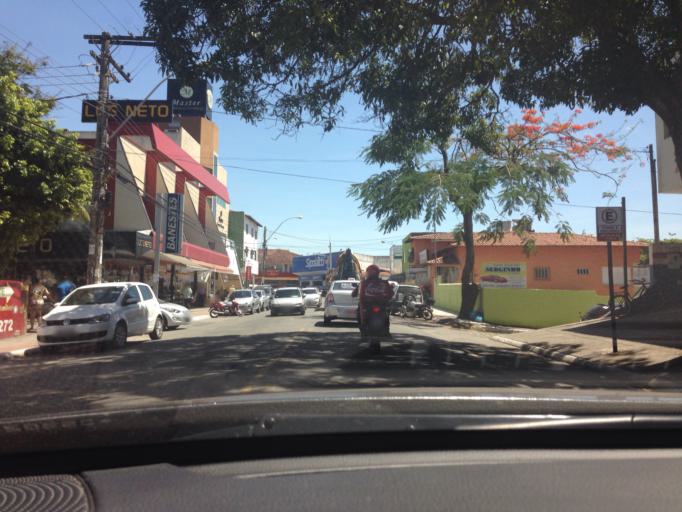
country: BR
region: Espirito Santo
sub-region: Guarapari
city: Guarapari
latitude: -20.6598
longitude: -40.4976
